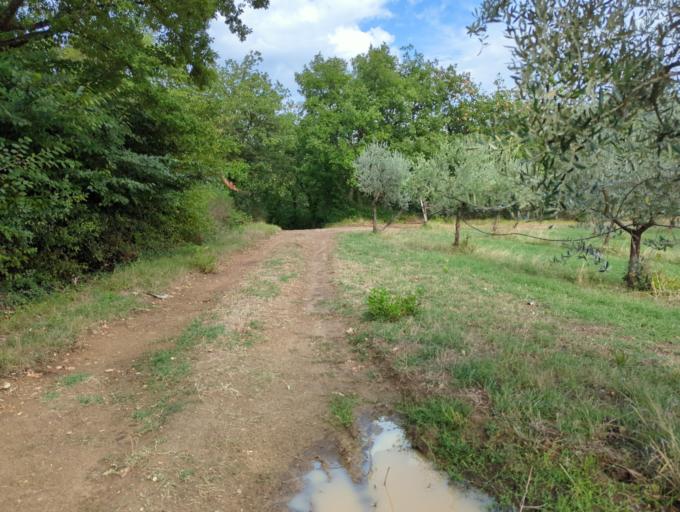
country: IT
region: Tuscany
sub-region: Province of Arezzo
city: Castiglion Fibocchi
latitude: 43.5438
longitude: 11.7668
